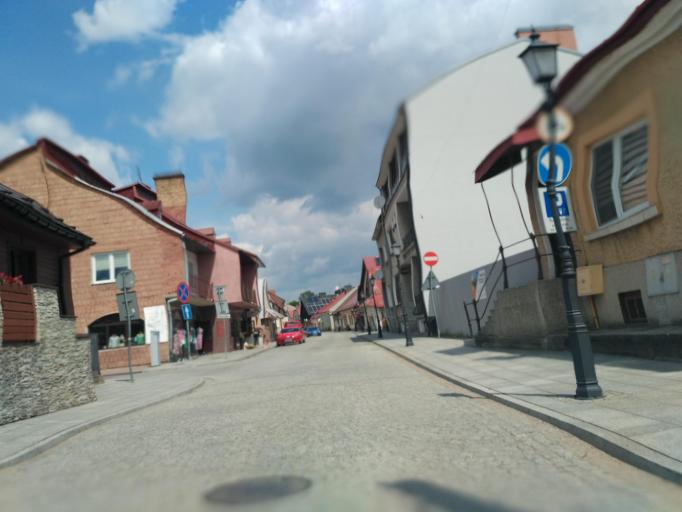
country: PL
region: Subcarpathian Voivodeship
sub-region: Powiat debicki
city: Pilzno
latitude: 49.9764
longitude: 21.2925
